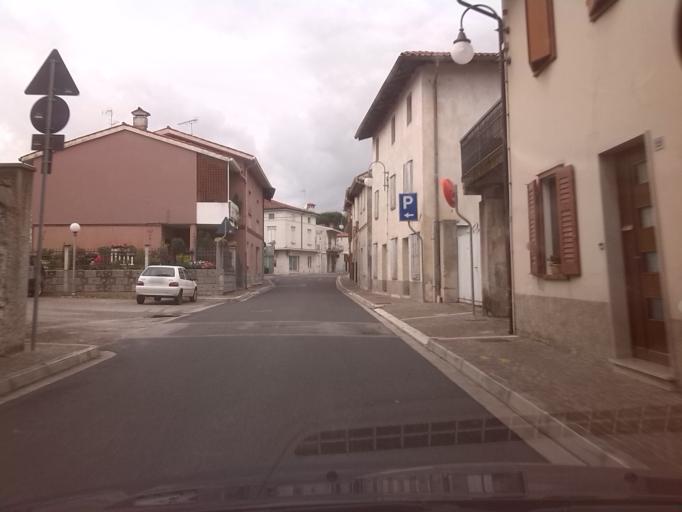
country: IT
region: Friuli Venezia Giulia
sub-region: Provincia di Gorizia
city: Farra d'Isonzo
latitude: 45.9065
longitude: 13.5190
